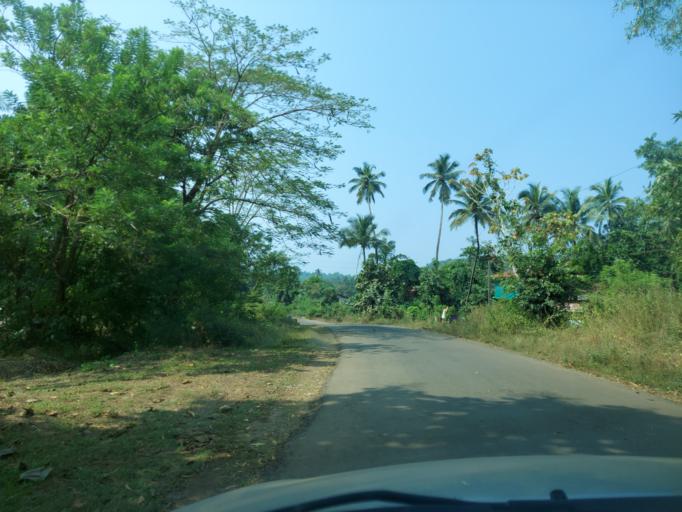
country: IN
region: Maharashtra
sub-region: Sindhudurg
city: Kudal
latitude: 15.9734
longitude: 73.6098
